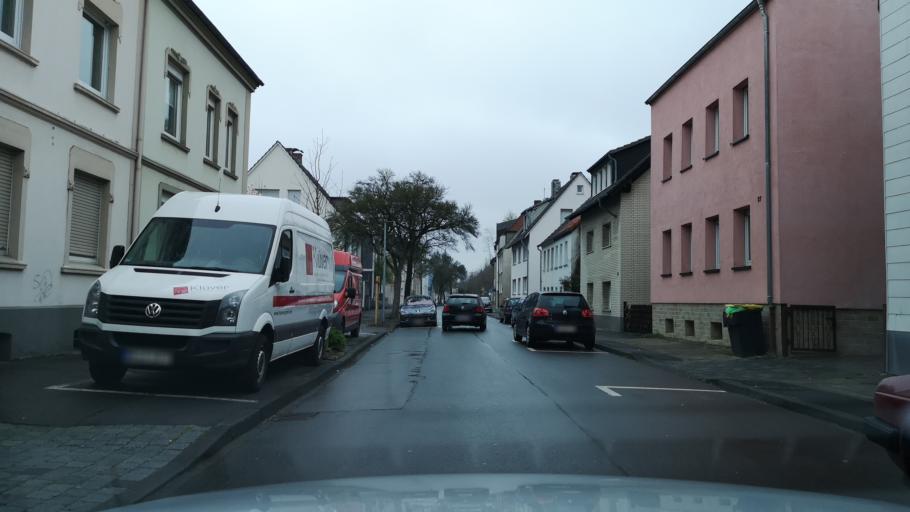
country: DE
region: North Rhine-Westphalia
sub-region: Regierungsbezirk Arnsberg
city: Menden
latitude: 51.4335
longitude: 7.8058
